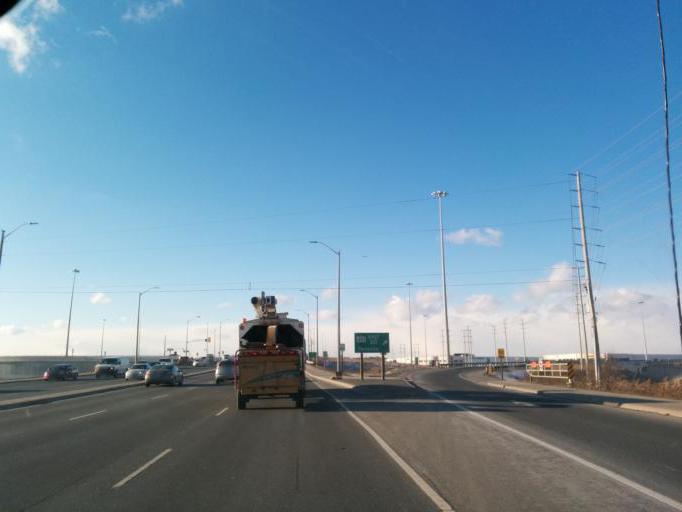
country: CA
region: Ontario
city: Mississauga
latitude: 43.6277
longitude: -79.6811
